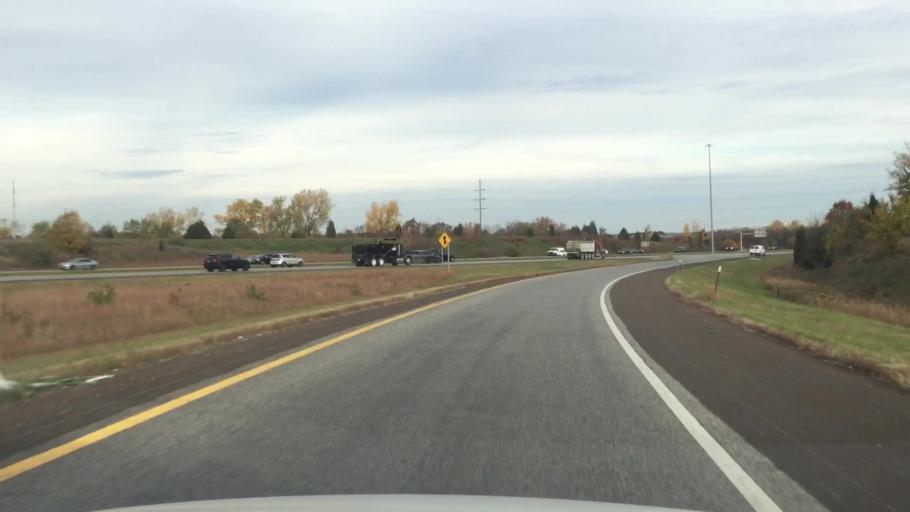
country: US
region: Kansas
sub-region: Wyandotte County
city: Edwardsville
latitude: 39.0137
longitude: -94.7842
